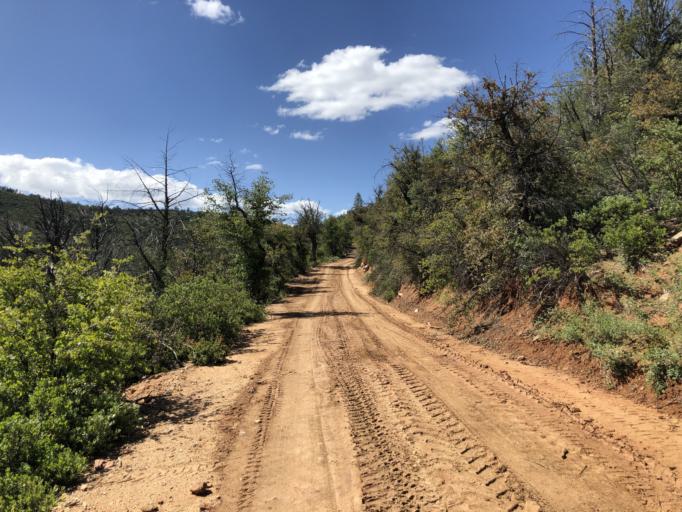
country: US
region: Arizona
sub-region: Gila County
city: Star Valley
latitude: 34.3539
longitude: -111.2793
